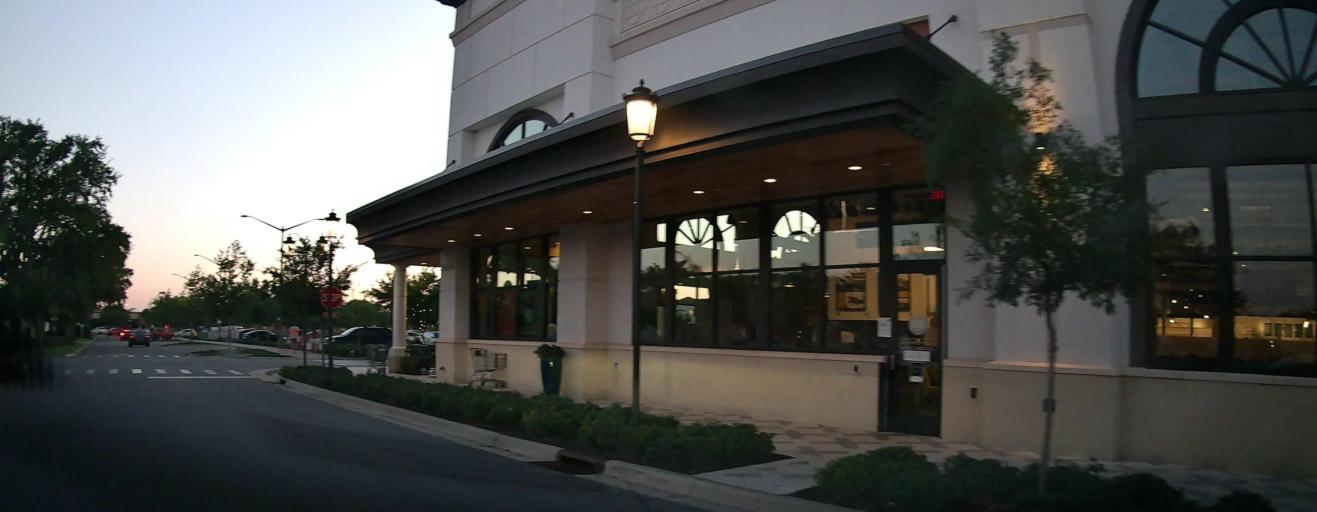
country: US
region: Florida
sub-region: Alachua County
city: Gainesville
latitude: 29.6253
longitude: -82.3759
